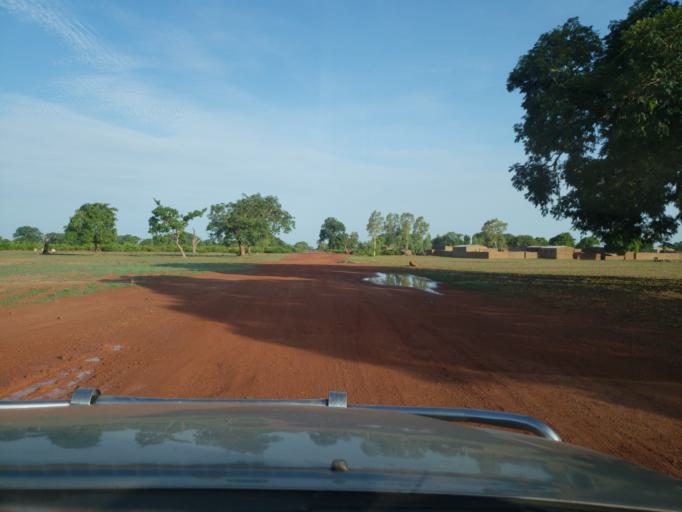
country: ML
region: Sikasso
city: Koutiala
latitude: 12.4170
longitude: -5.5728
